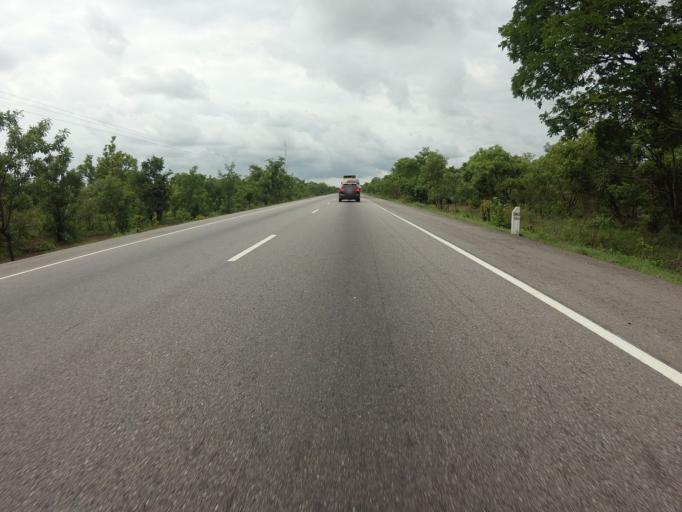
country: GH
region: Northern
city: Tamale
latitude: 9.0569
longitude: -1.3141
